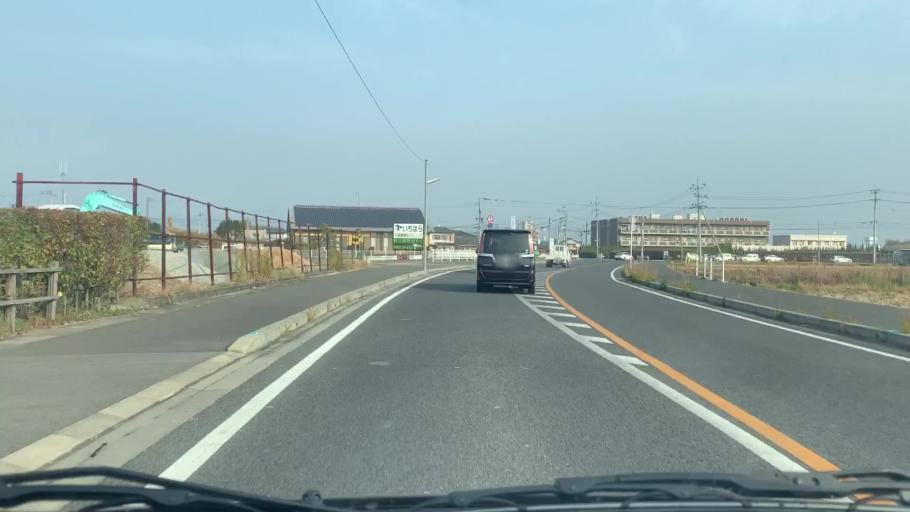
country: JP
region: Saga Prefecture
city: Saga-shi
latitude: 33.2370
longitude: 130.2580
